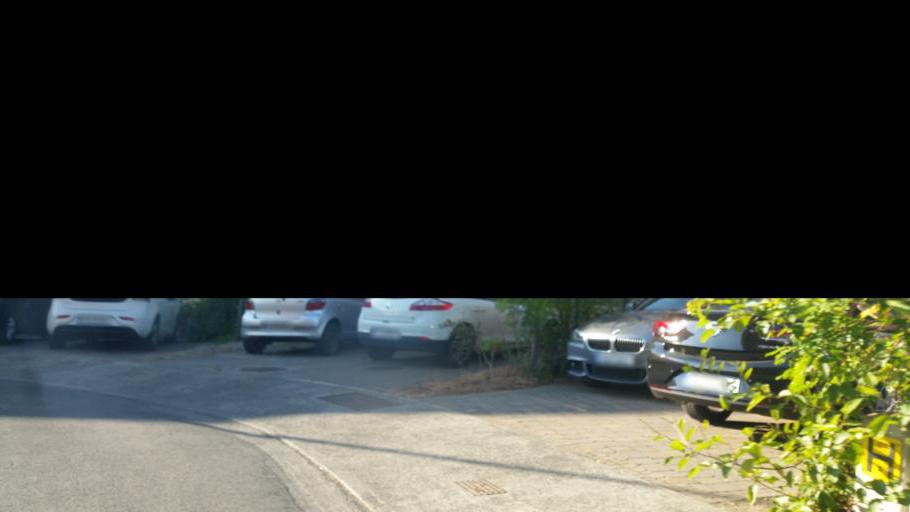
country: IE
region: Leinster
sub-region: Fingal County
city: Blanchardstown
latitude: 53.4290
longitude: -6.3755
